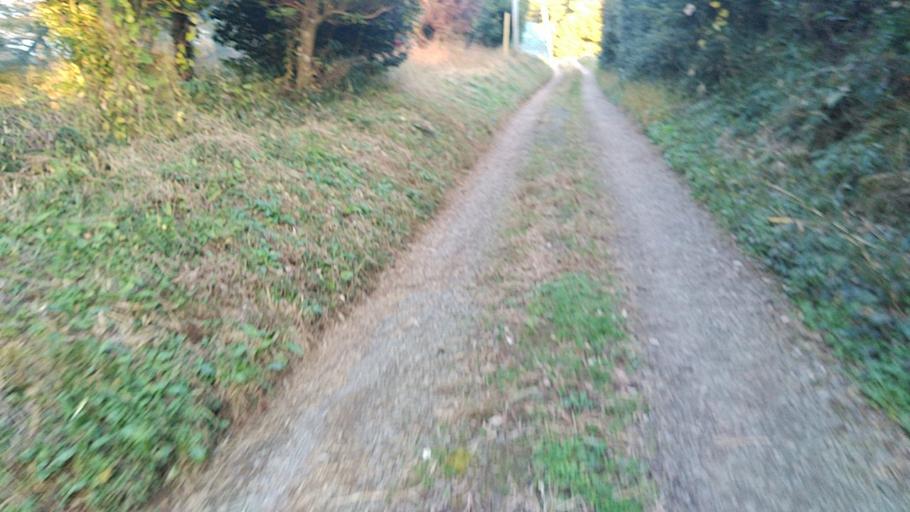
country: JP
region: Chiba
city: Sawara
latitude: 35.8220
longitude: 140.5078
